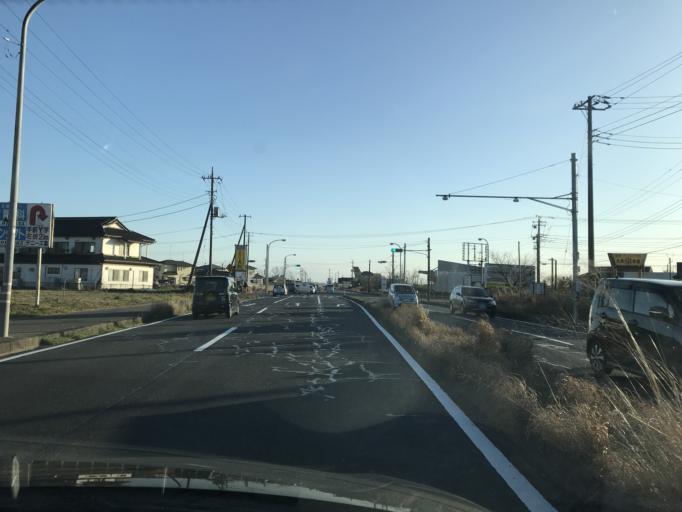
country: JP
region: Chiba
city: Omigawa
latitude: 35.8890
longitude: 140.6324
